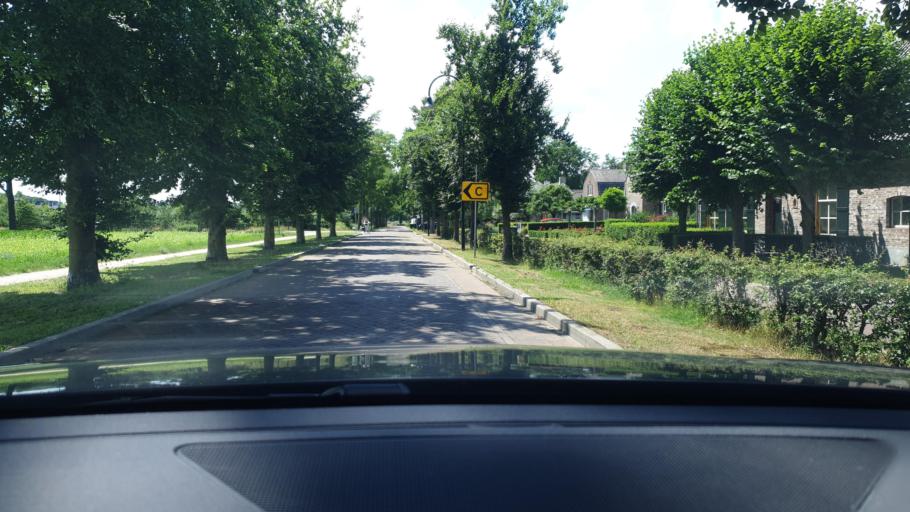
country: NL
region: North Brabant
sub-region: Gemeente Uden
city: Uden
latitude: 51.6546
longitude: 5.6055
